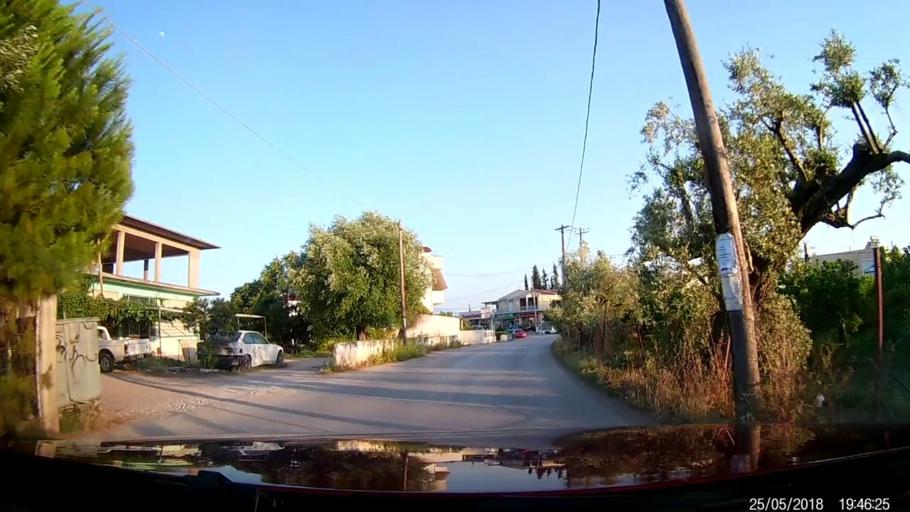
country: GR
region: Central Greece
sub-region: Nomos Evvoias
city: Ayios Nikolaos
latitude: 38.4269
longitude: 23.6402
